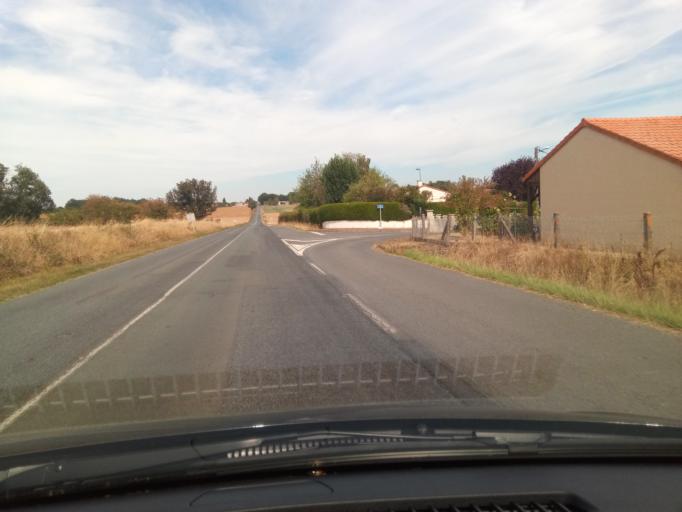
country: FR
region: Poitou-Charentes
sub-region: Departement de la Vienne
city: Terce
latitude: 46.5211
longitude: 0.5668
